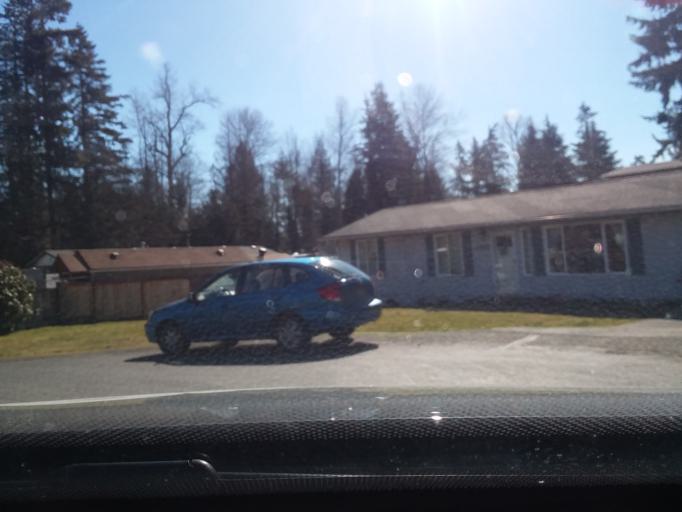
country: US
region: Washington
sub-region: Pierce County
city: Summit
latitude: 47.1632
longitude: -122.3425
